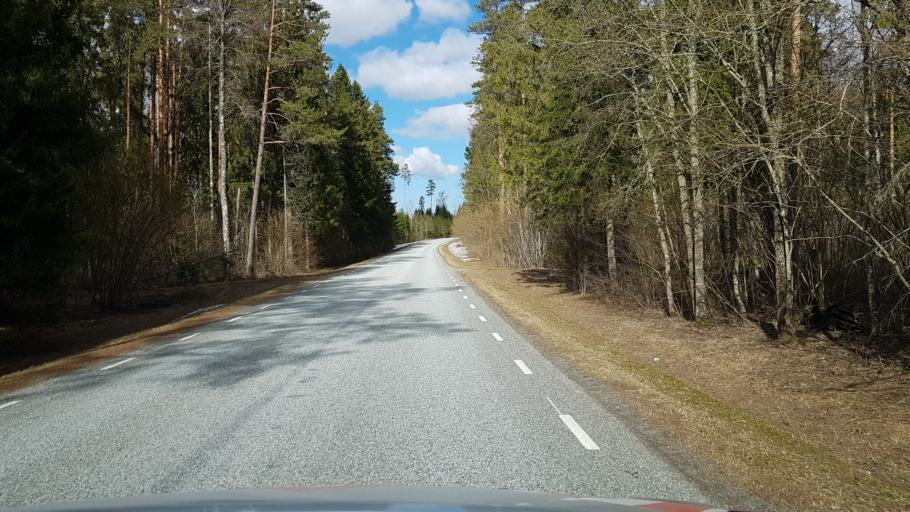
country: EE
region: Laeaene-Virumaa
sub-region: Tamsalu vald
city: Tamsalu
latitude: 59.2349
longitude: 26.1723
